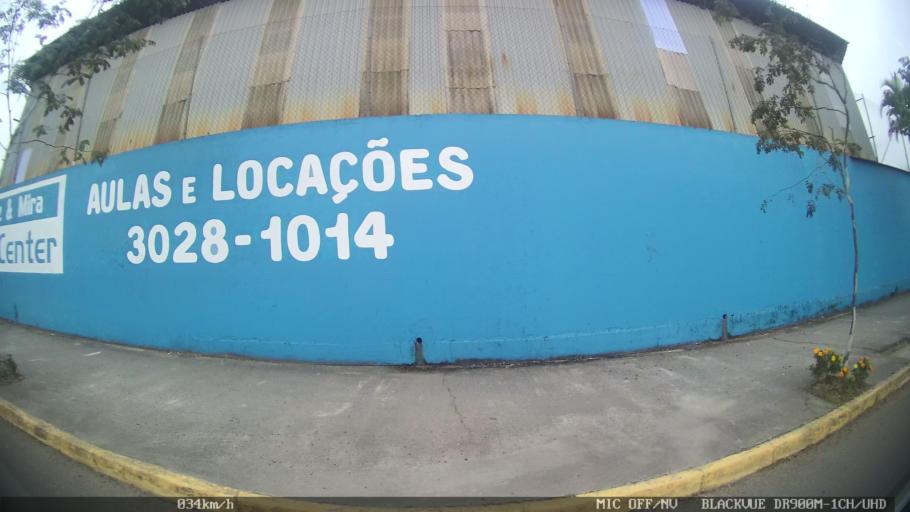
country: BR
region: Santa Catarina
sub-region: Joinville
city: Joinville
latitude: -26.2947
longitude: -48.8647
